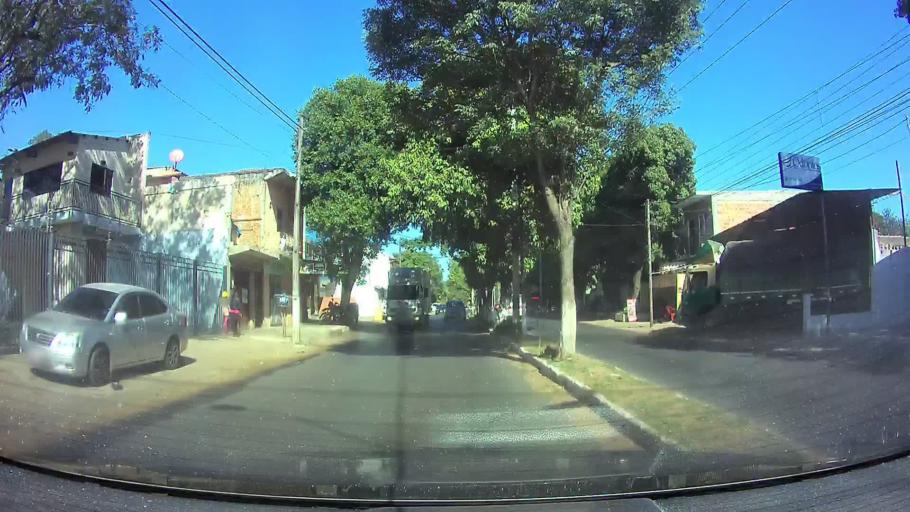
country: PY
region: Central
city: Villa Elisa
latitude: -25.3639
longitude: -57.5772
